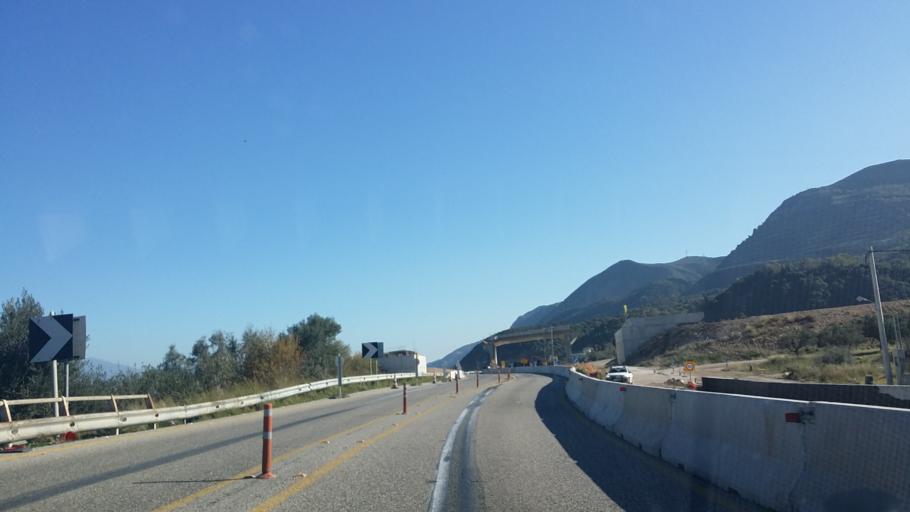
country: GR
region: West Greece
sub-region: Nomos Achaias
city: Ano Kastritsion
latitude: 38.3243
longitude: 21.8536
